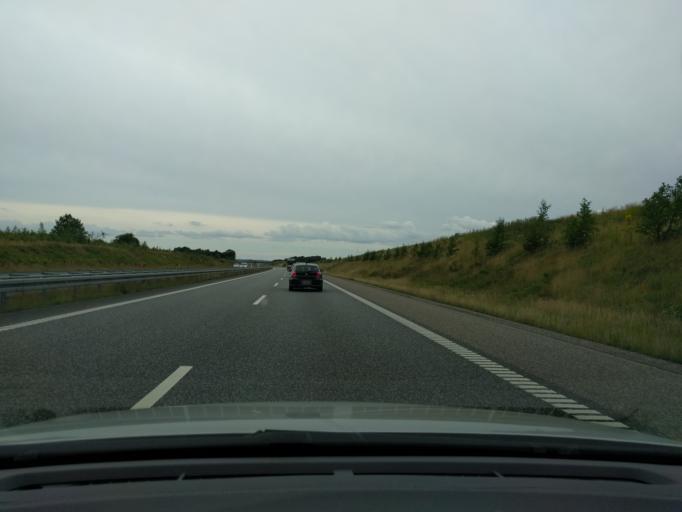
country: DK
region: Central Jutland
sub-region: Hedensted Kommune
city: Torring
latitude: 55.8221
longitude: 9.5410
